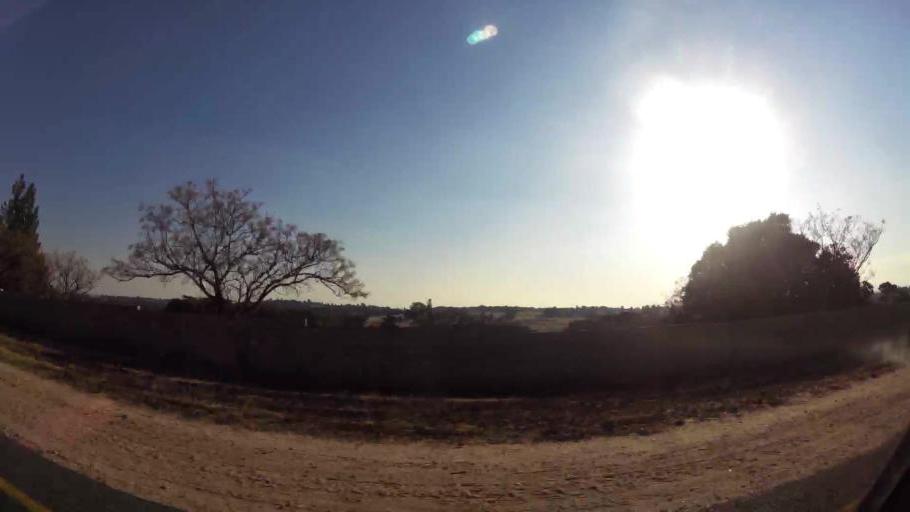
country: ZA
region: Gauteng
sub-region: West Rand District Municipality
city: Muldersdriseloop
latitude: -26.0265
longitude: 27.9084
